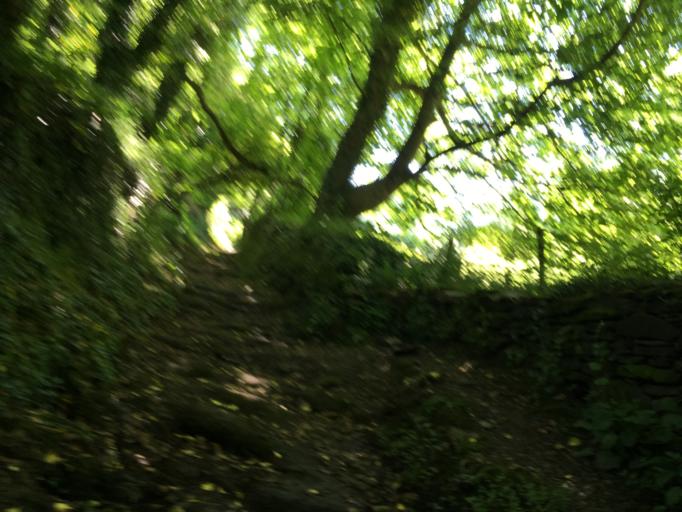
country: GB
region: England
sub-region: Devon
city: Dartmouth
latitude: 50.3455
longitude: -3.5509
